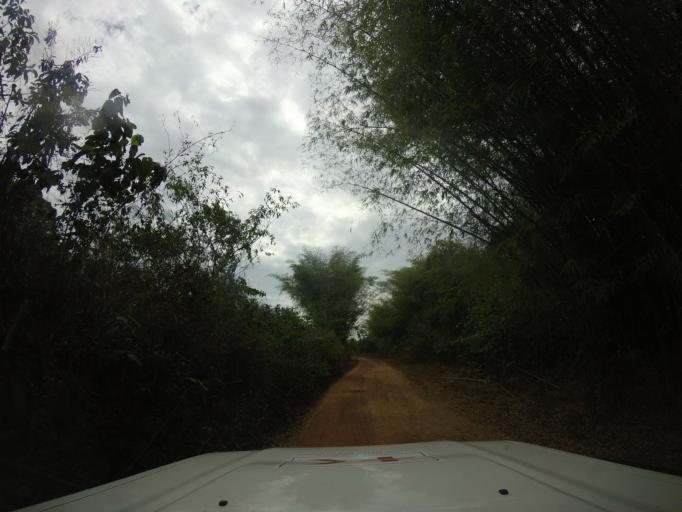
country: SL
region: Southern Province
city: Zimmi
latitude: 7.2114
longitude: -11.1994
